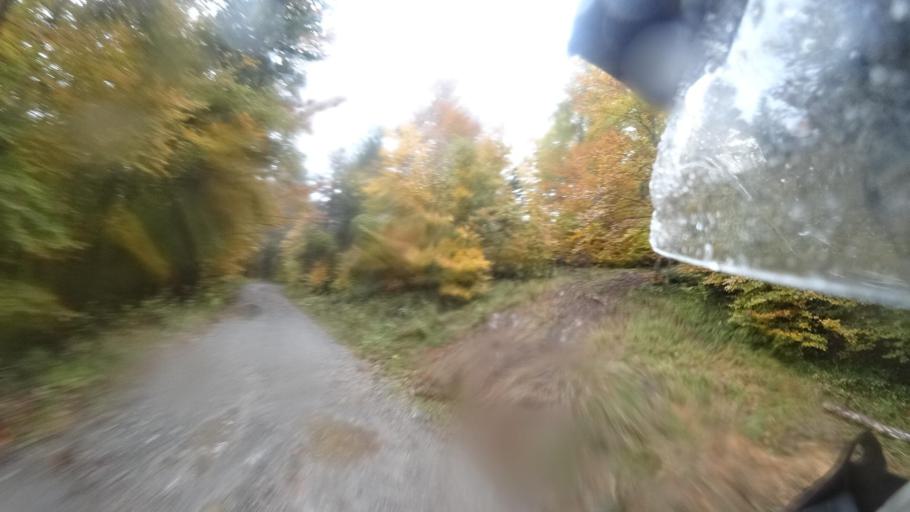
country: HR
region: Primorsko-Goranska
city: Vrbovsko
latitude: 45.3528
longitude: 15.0726
